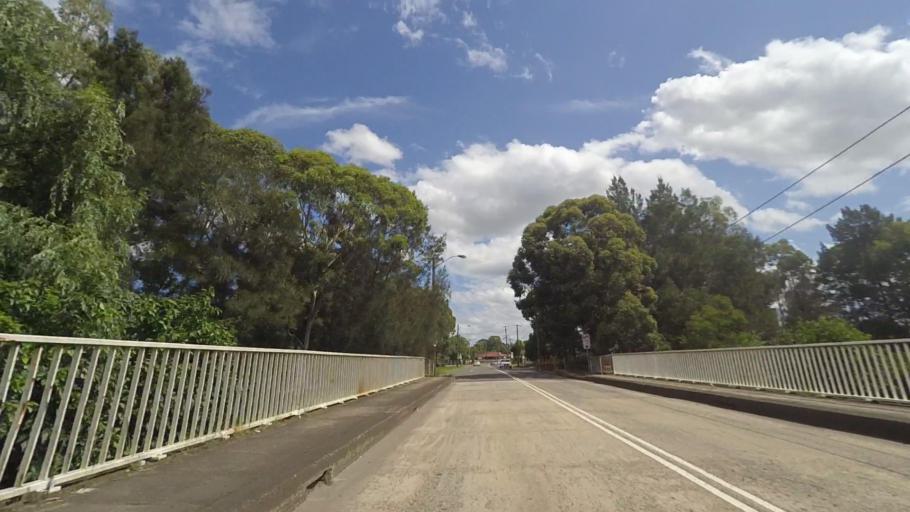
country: AU
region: New South Wales
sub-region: Fairfield
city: Fairfield East
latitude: -33.8605
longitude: 150.9579
